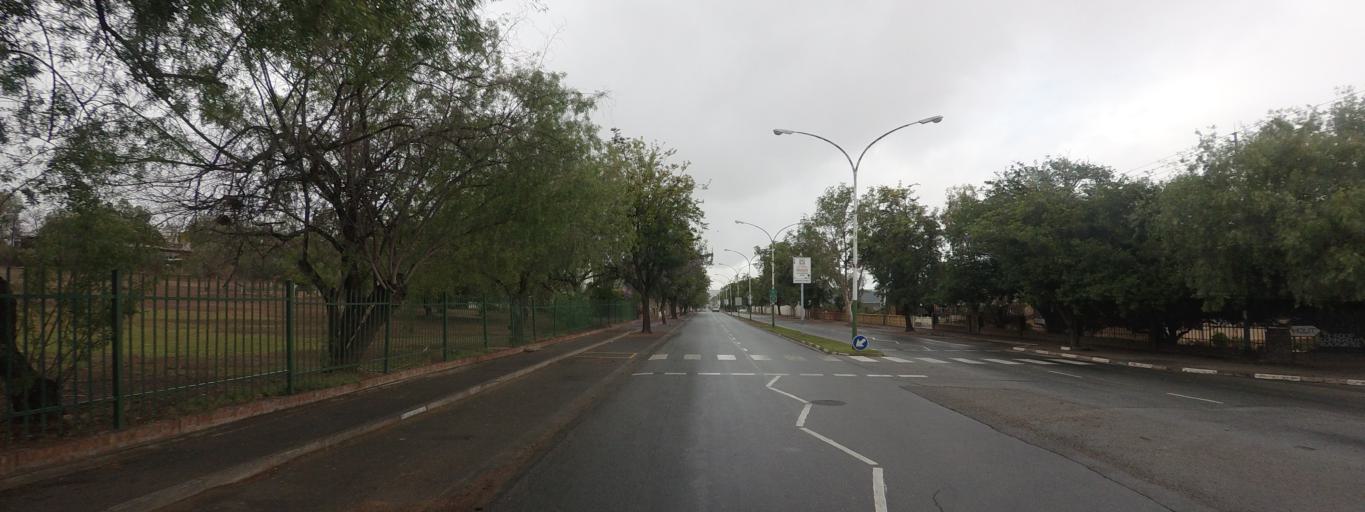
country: ZA
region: Western Cape
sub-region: Eden District Municipality
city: Oudtshoorn
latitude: -33.5962
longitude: 22.2044
